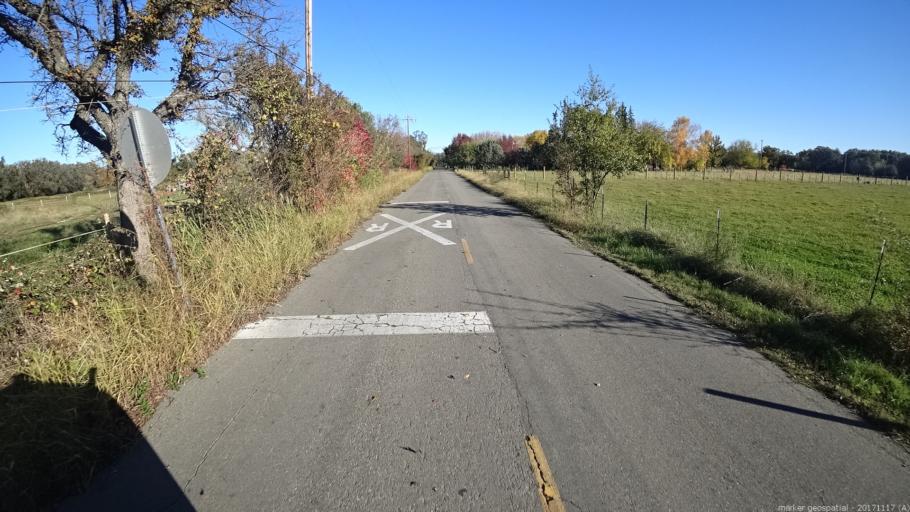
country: US
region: California
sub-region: Shasta County
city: Cottonwood
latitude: 40.3893
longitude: -122.2655
